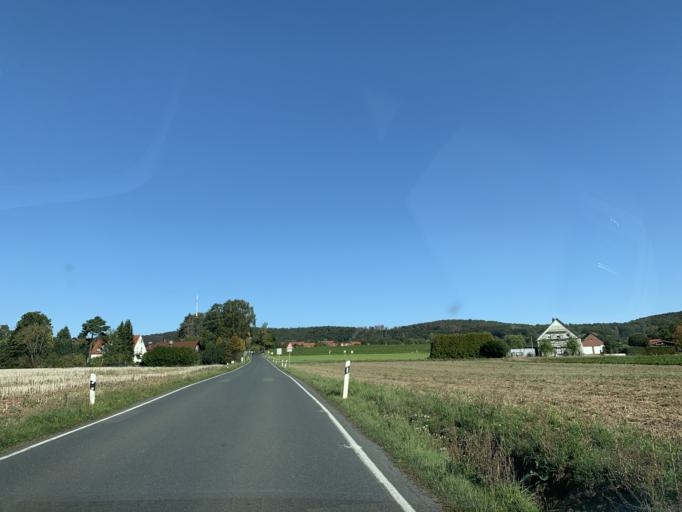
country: DE
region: North Rhine-Westphalia
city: Porta Westfalica
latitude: 52.2252
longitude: 8.9452
